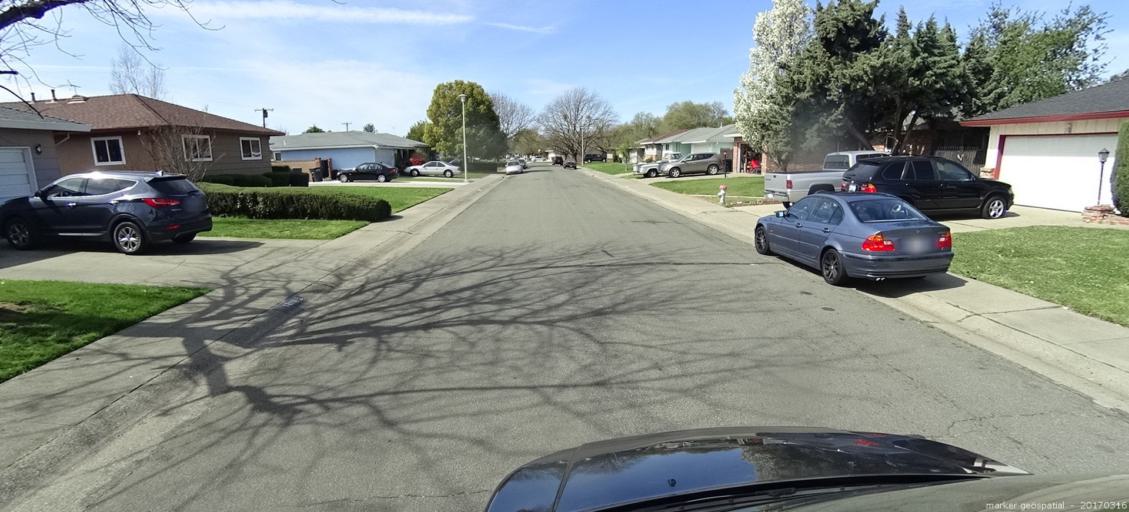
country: US
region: California
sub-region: Sacramento County
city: Parkway
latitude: 38.4973
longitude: -121.4963
